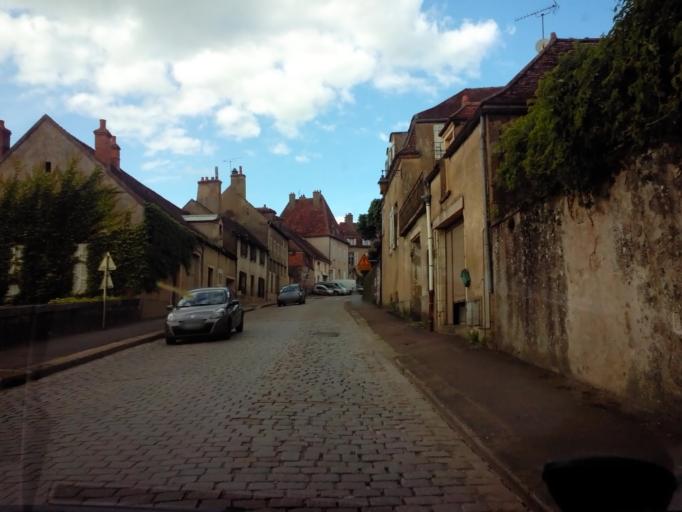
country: FR
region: Bourgogne
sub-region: Departement de la Cote-d'Or
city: Semur-en-Auxois
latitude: 47.4915
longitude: 4.3309
